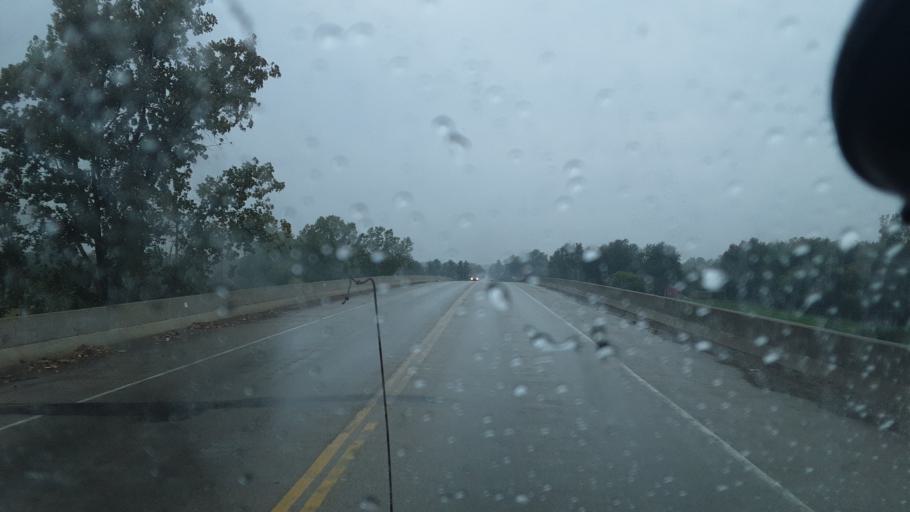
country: US
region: Ohio
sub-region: Crawford County
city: Crestline
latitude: 40.7871
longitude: -82.7167
